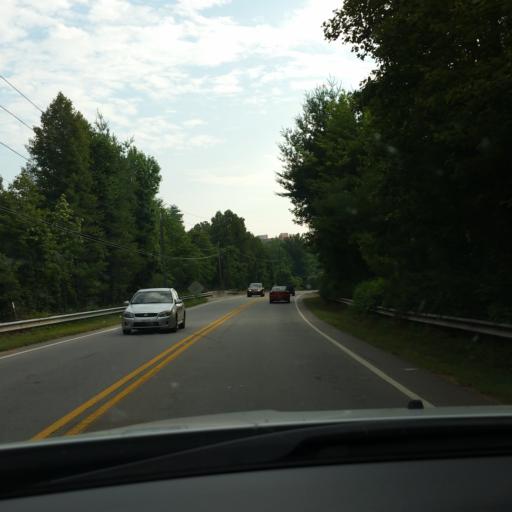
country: US
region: North Carolina
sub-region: Buncombe County
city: Bent Creek
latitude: 35.5375
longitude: -82.6597
